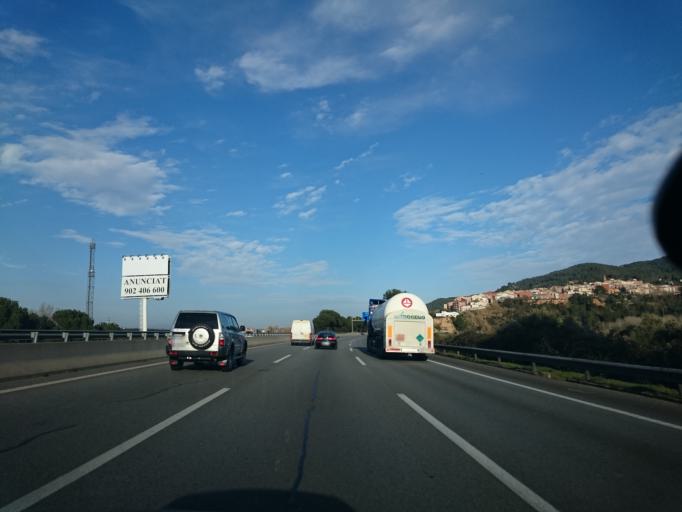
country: ES
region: Catalonia
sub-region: Provincia de Barcelona
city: Gelida
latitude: 41.4421
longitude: 1.8479
